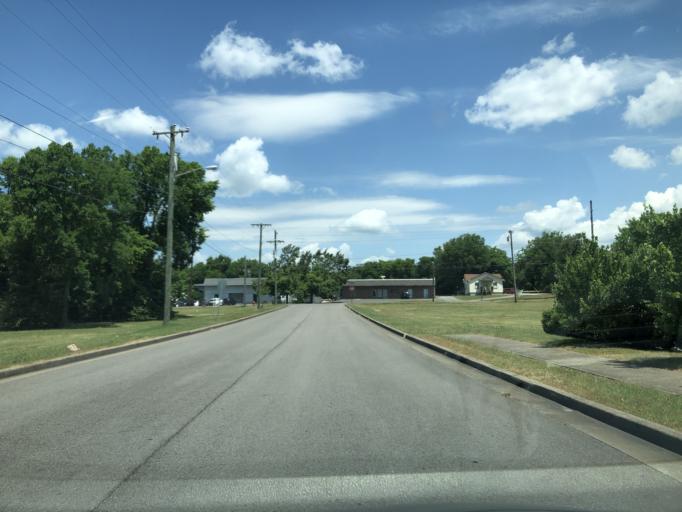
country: US
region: Tennessee
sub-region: Davidson County
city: Goodlettsville
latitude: 36.2623
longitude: -86.6981
